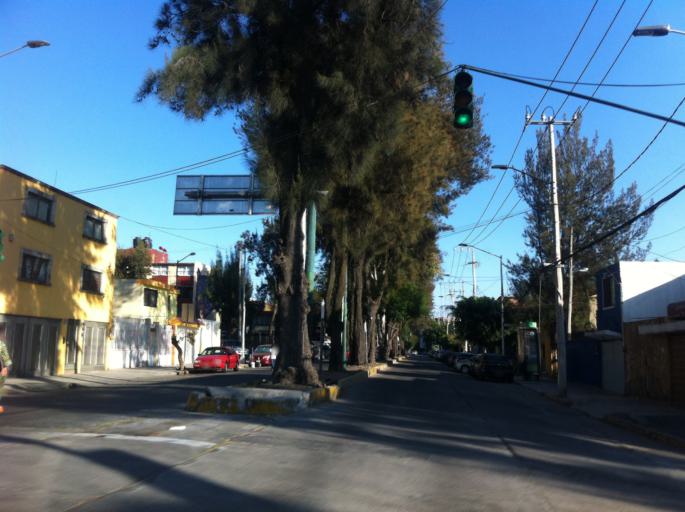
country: MX
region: Mexico City
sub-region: Iztacalco
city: Iztacalco
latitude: 19.4115
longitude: -99.1015
